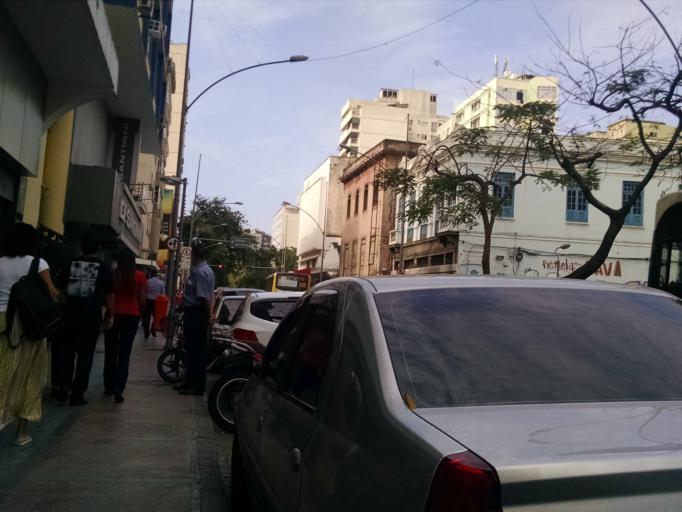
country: BR
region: Rio de Janeiro
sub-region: Rio De Janeiro
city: Rio de Janeiro
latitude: -22.9293
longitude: -43.1774
